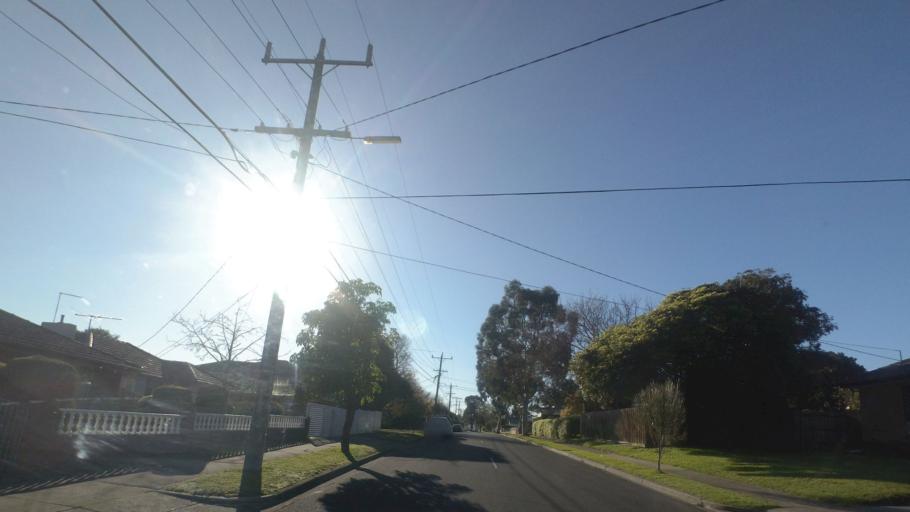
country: AU
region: Victoria
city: Watsonia
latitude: -37.7207
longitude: 145.0770
